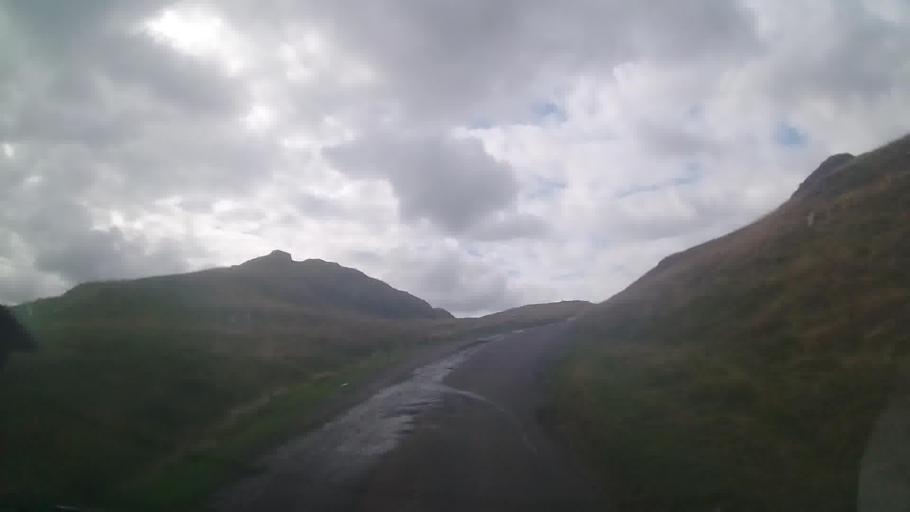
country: GB
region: England
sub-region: Cumbria
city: Keswick
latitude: 54.4030
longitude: -3.1811
